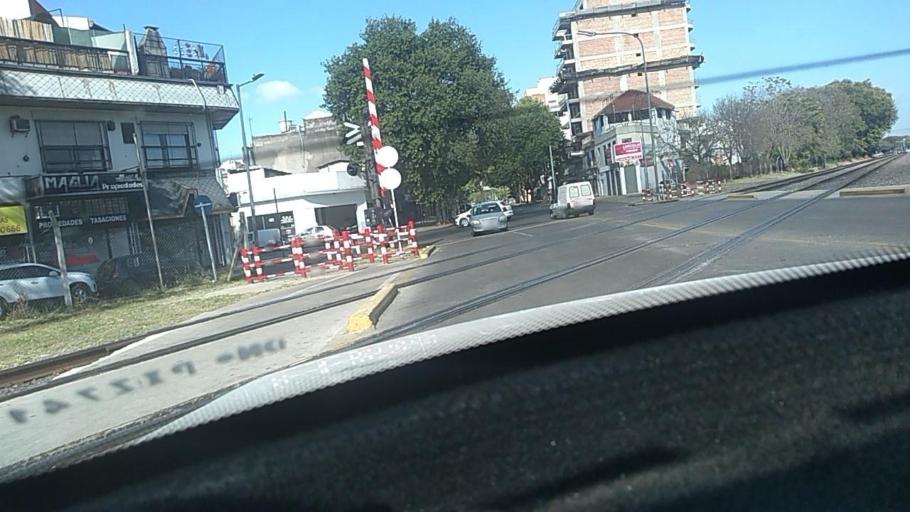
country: AR
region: Buenos Aires F.D.
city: Villa Santa Rita
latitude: -34.6023
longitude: -58.5057
